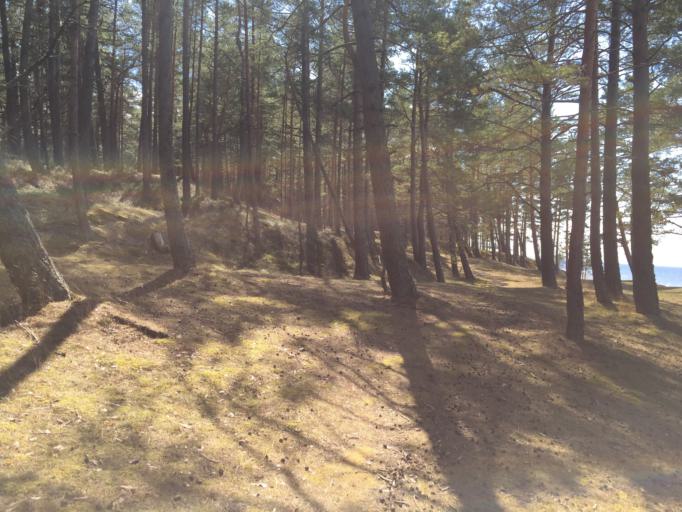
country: LV
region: Saulkrastu
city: Saulkrasti
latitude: 57.2282
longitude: 24.3850
